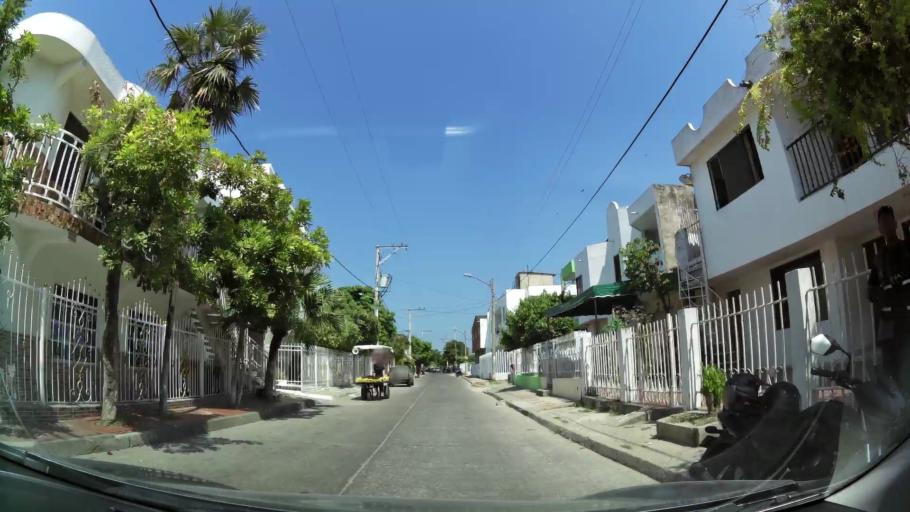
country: CO
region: Bolivar
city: Cartagena
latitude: 10.4024
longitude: -75.4914
